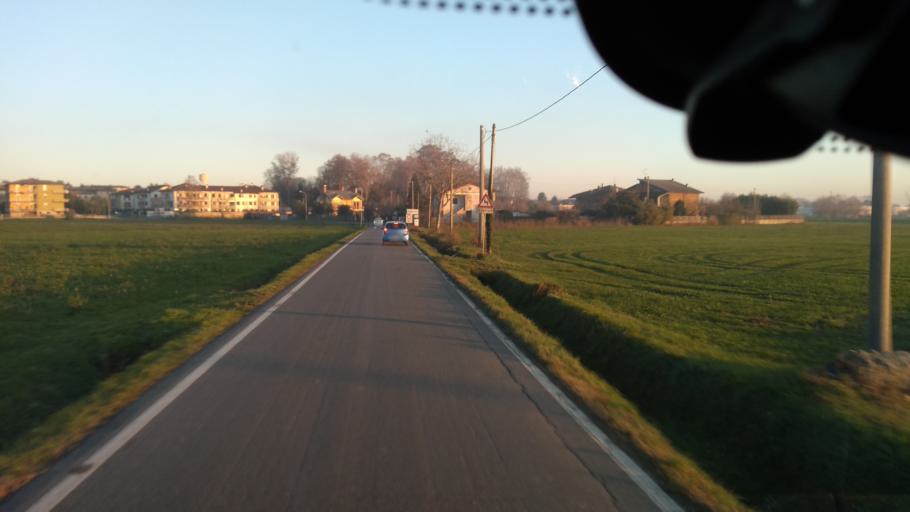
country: IT
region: Lombardy
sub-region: Provincia di Bergamo
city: Casirate d'Adda
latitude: 45.4957
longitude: 9.5600
